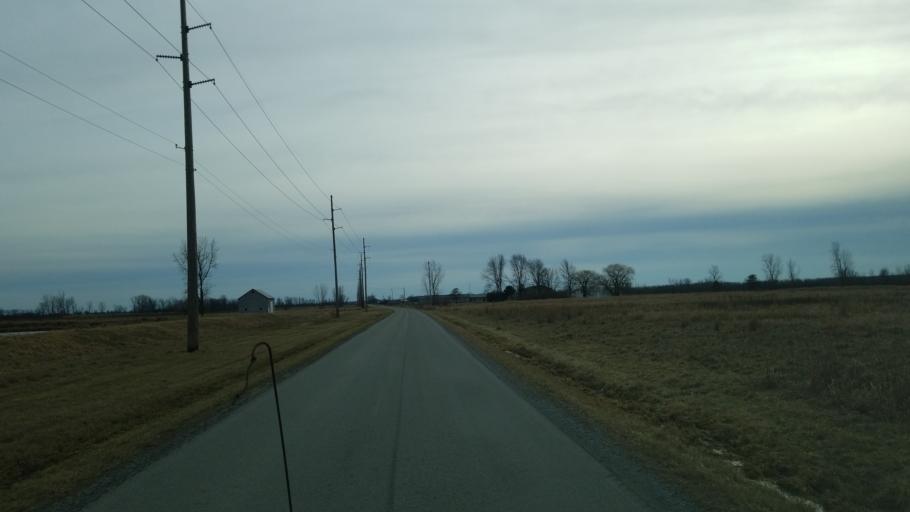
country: US
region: Ohio
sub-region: Wyandot County
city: Upper Sandusky
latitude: 40.7186
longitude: -83.2995
